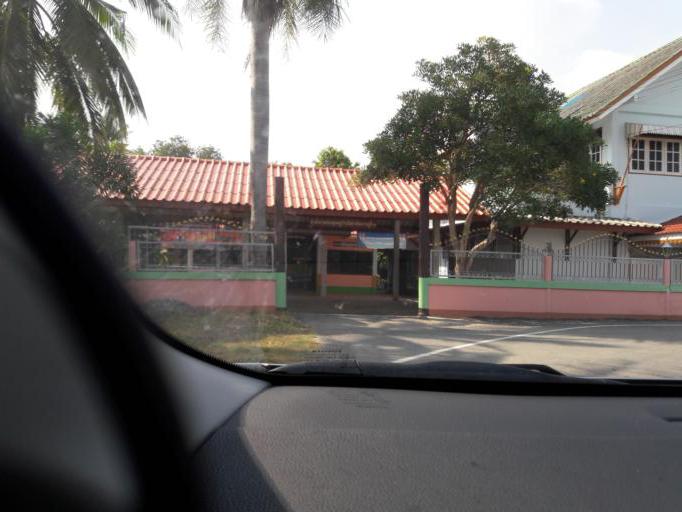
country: TH
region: Ang Thong
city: Wiset Chaichan
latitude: 14.5342
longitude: 100.3854
